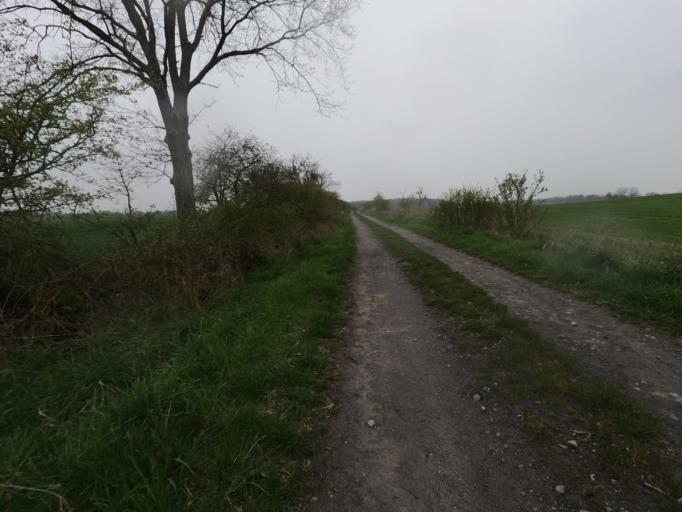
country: PL
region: West Pomeranian Voivodeship
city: Trzcinsko Zdroj
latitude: 52.9219
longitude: 14.7306
